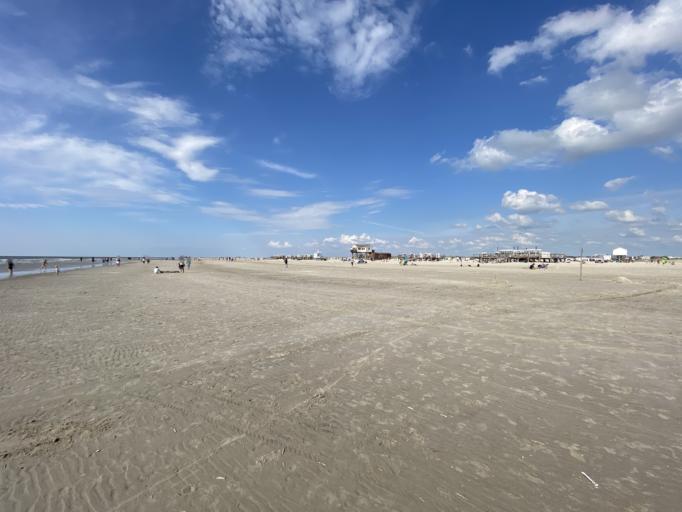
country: DE
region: Schleswig-Holstein
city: Sankt Peter-Ording
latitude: 54.3111
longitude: 8.5848
